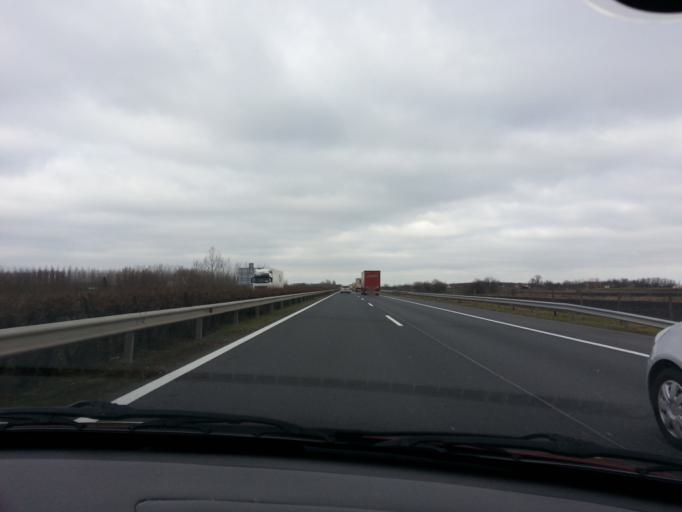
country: HU
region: Bacs-Kiskun
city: Kiskunfelegyhaza
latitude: 46.6886
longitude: 19.8136
